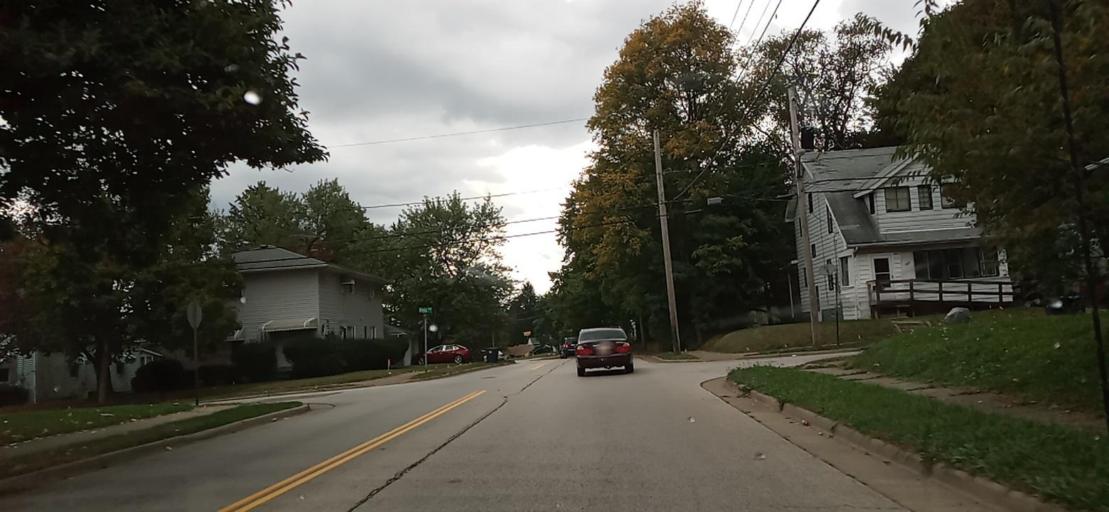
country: US
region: Ohio
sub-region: Summit County
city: Akron
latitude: 41.0652
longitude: -81.5583
